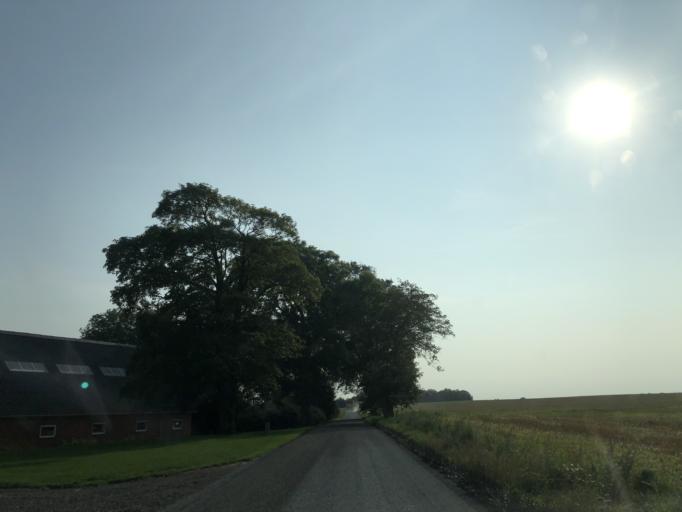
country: DK
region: Central Jutland
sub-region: Favrskov Kommune
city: Hammel
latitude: 56.2397
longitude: 9.7602
